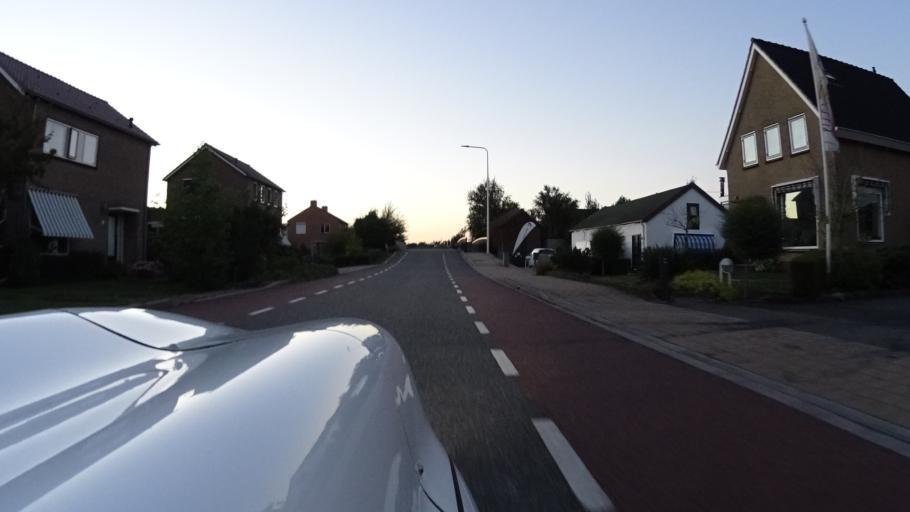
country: NL
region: South Holland
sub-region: Gemeente Kaag en Braassem
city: Oude Wetering
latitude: 52.1922
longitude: 4.6199
